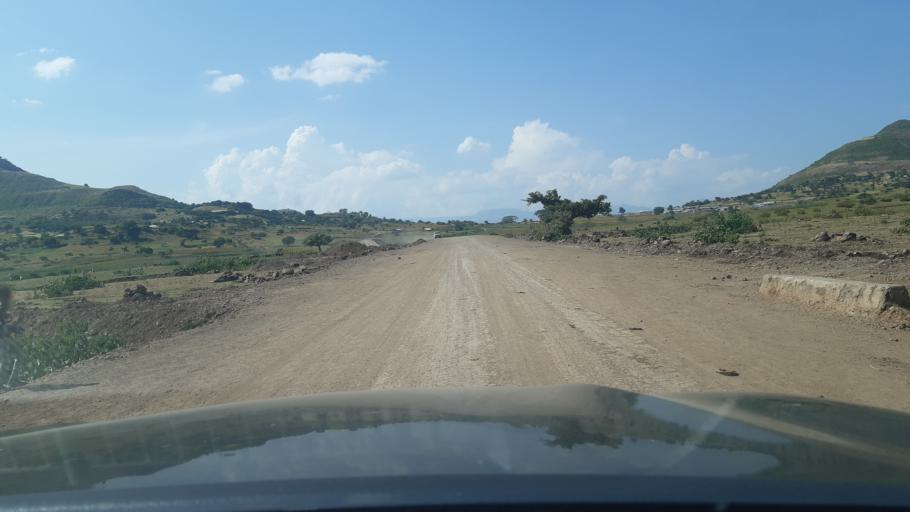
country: ET
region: Amhara
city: Dabat
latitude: 13.1552
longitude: 37.6140
